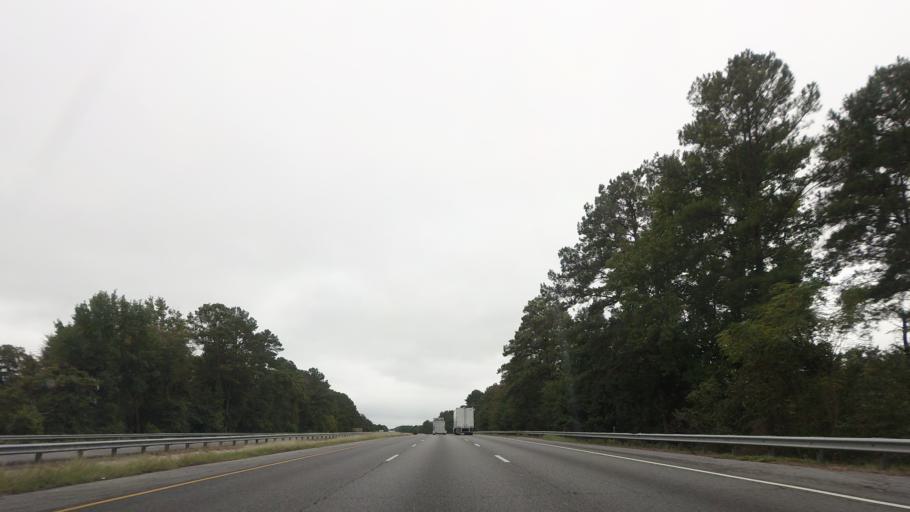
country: US
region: Georgia
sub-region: Houston County
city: Perry
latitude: 32.4143
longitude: -83.7627
